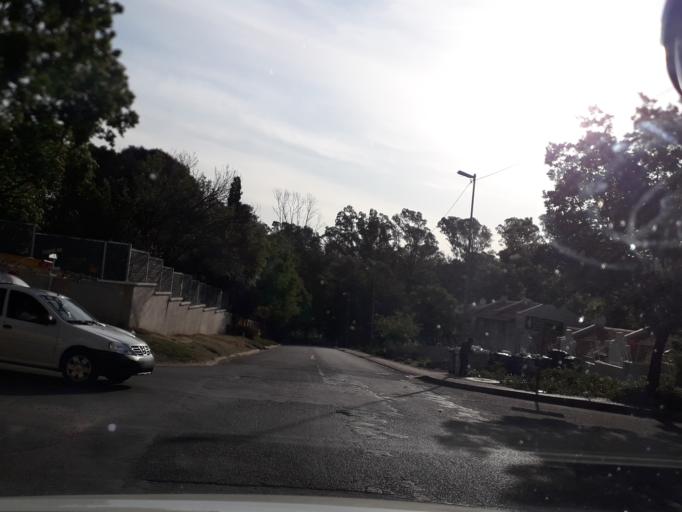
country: ZA
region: Gauteng
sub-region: City of Johannesburg Metropolitan Municipality
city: Diepsloot
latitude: -26.0521
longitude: 27.9900
